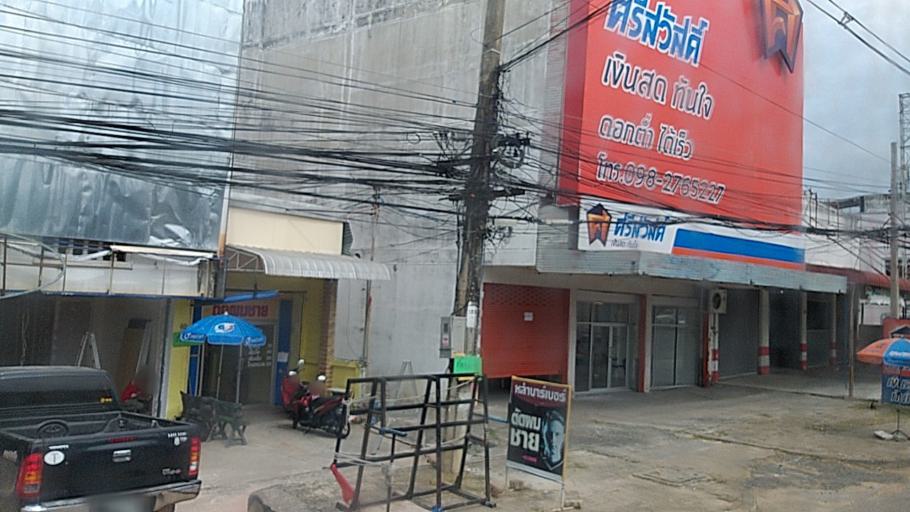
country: TH
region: Roi Et
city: Roi Et
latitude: 16.0601
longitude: 103.6278
